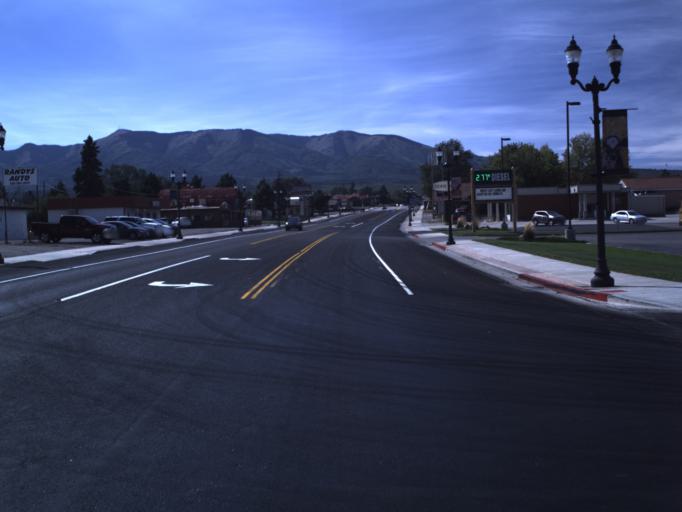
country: US
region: Utah
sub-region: San Juan County
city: Monticello
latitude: 37.8727
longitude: -109.3373
